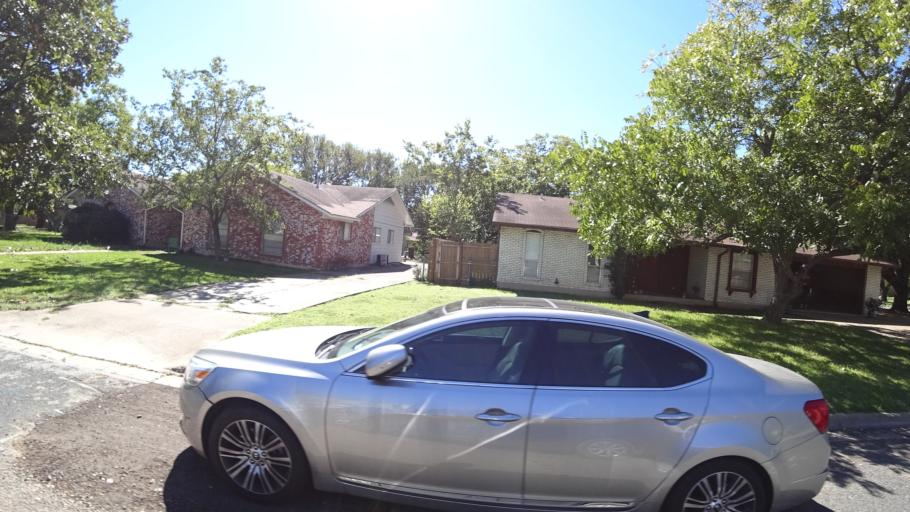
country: US
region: Texas
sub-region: Travis County
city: Rollingwood
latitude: 30.2280
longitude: -97.8016
